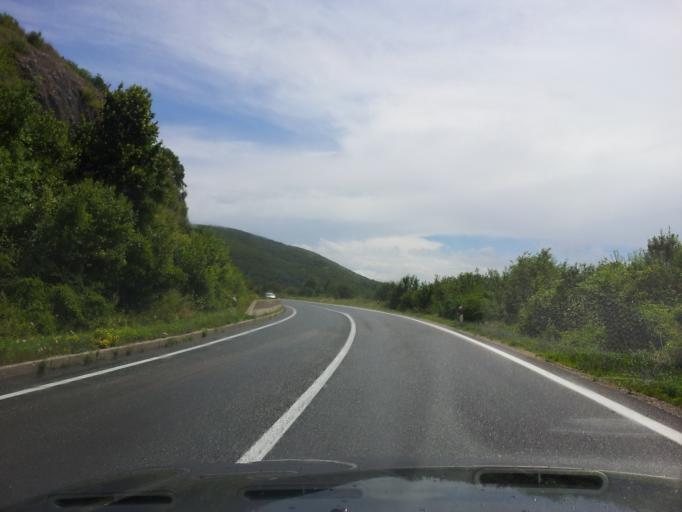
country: BA
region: Federation of Bosnia and Herzegovina
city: Bihac
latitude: 44.6194
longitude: 15.7368
